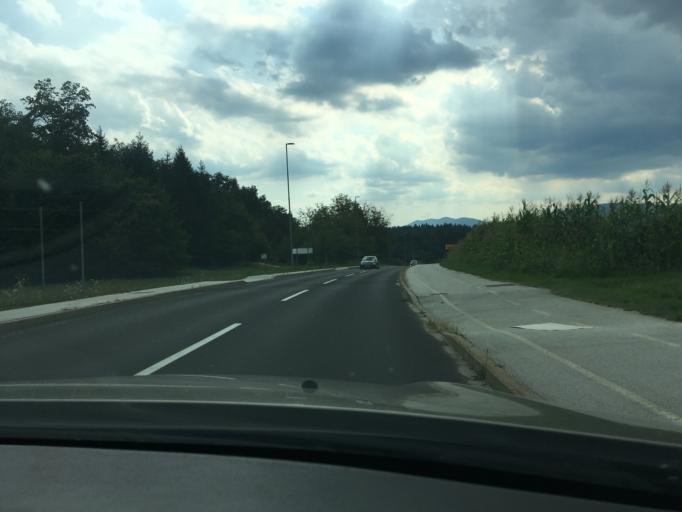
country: SI
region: Novo Mesto
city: Novo Mesto
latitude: 45.7959
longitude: 15.1468
